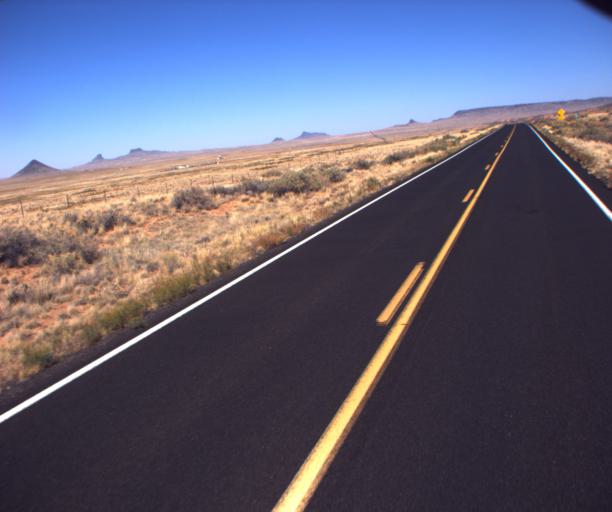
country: US
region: Arizona
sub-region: Navajo County
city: Dilkon
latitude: 35.3001
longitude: -110.4239
